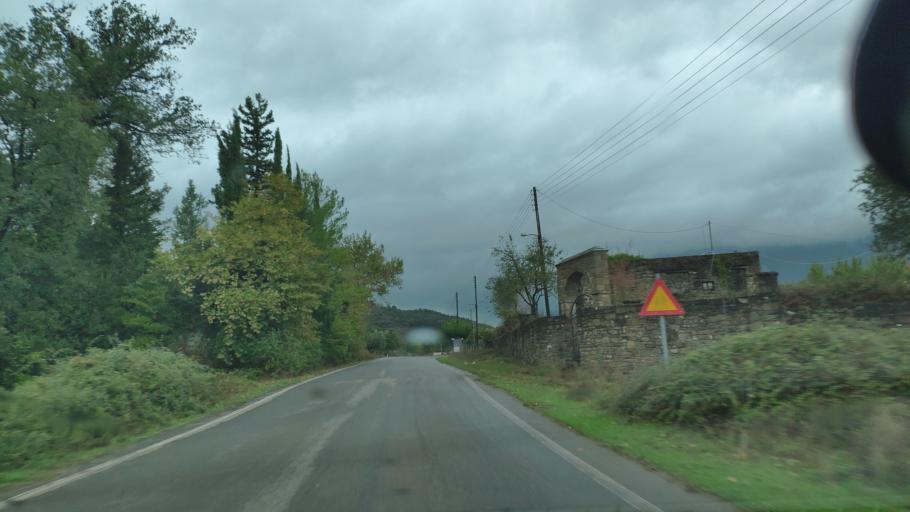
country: GR
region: West Greece
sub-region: Nomos Aitolias kai Akarnanias
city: Krikellos
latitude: 39.0012
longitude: 21.3100
